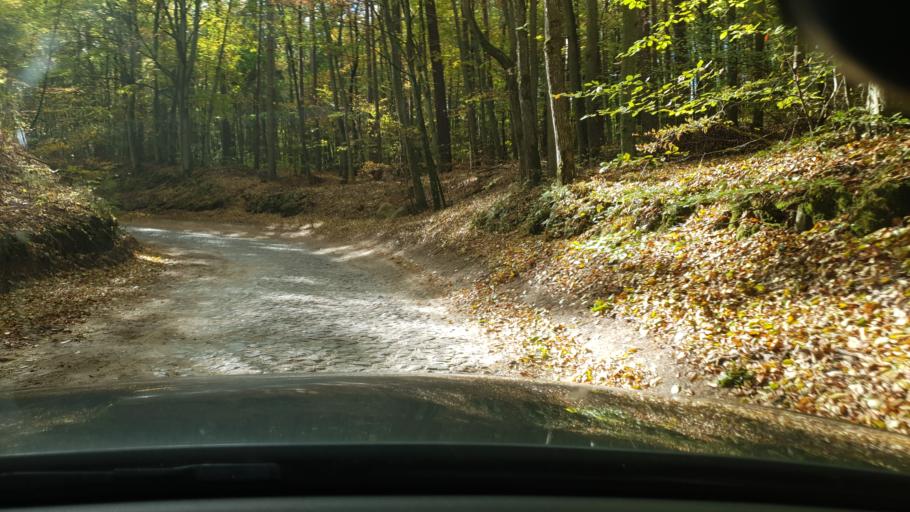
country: PL
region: Pomeranian Voivodeship
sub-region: Powiat wejherowski
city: Reda
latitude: 54.5861
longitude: 18.3181
